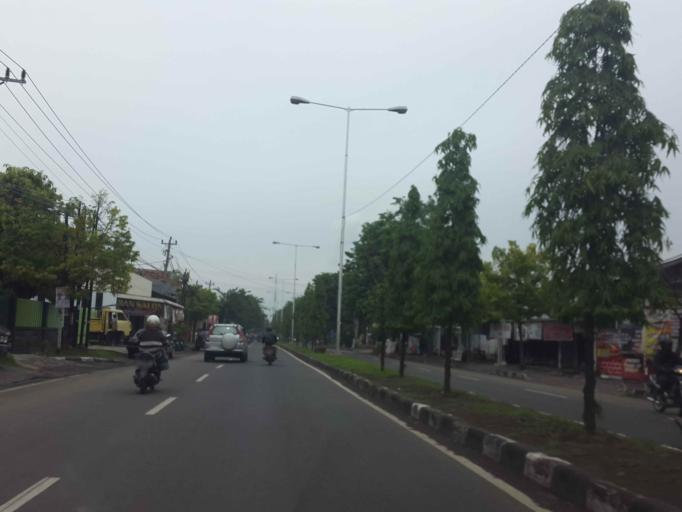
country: ID
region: Central Java
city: Semarang
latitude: -7.0021
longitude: 110.4675
